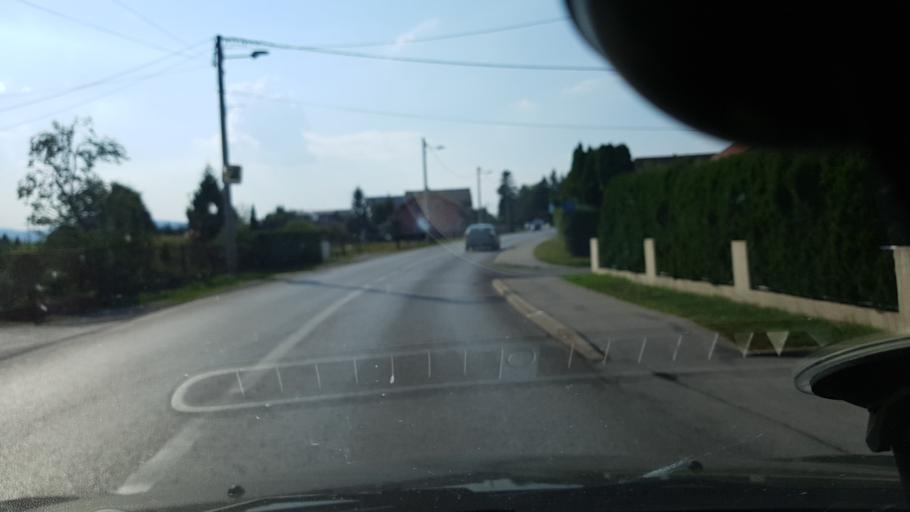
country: HR
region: Zagrebacka
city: Brdovec
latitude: 45.8668
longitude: 15.7627
